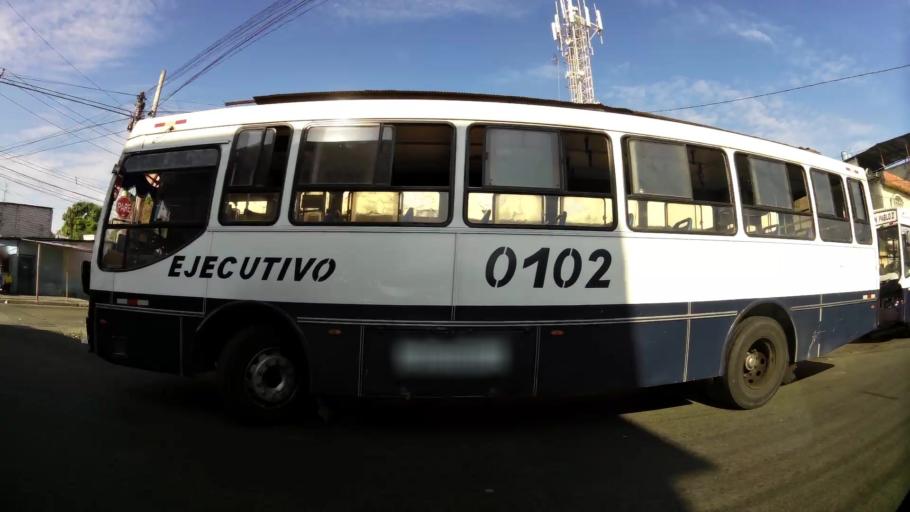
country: EC
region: Guayas
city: Guayaquil
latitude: -2.2137
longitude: -79.9269
